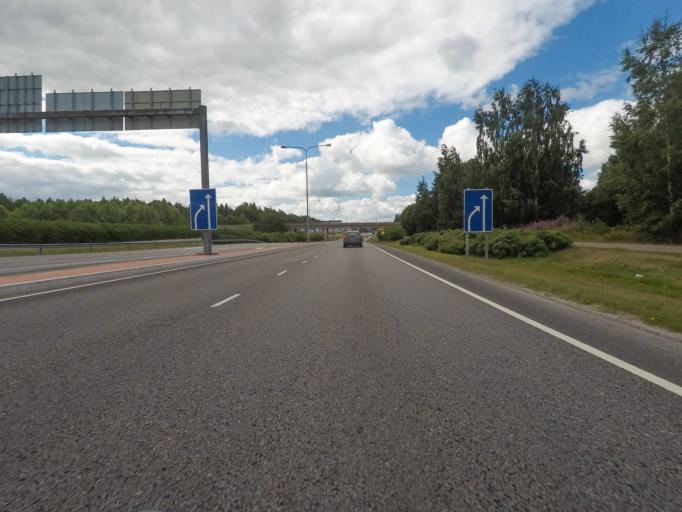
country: FI
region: Varsinais-Suomi
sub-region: Turku
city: Raisio
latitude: 60.4763
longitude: 22.1562
